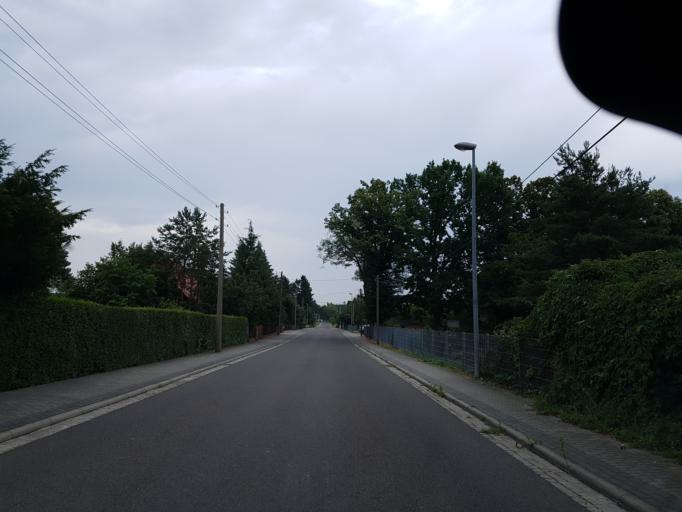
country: DE
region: Brandenburg
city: Schipkau
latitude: 51.5493
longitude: 13.9210
